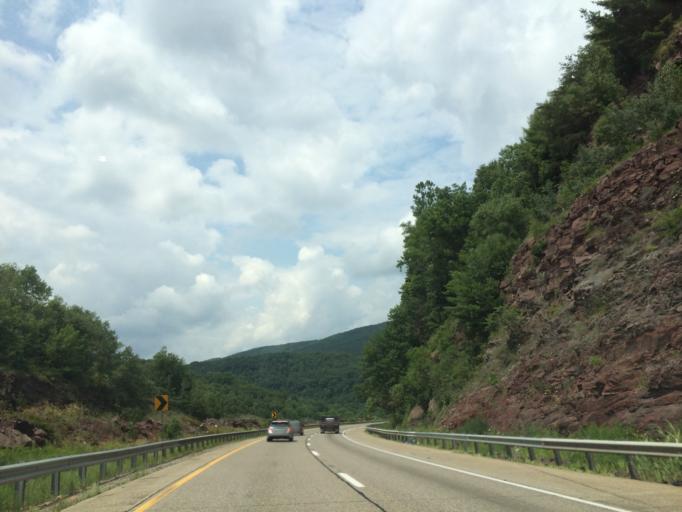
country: US
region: Pennsylvania
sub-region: Luzerne County
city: Nescopeck
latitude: 41.0038
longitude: -76.1600
